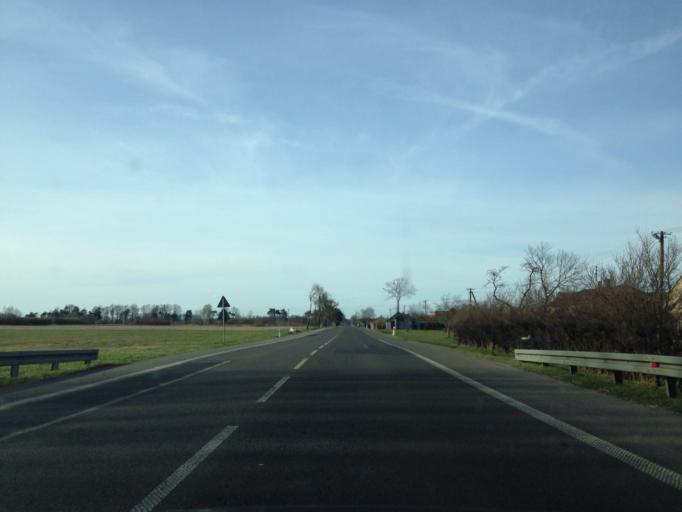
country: PL
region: Lodz Voivodeship
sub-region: Powiat kutnowski
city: Ostrowy
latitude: 52.3265
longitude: 19.1515
